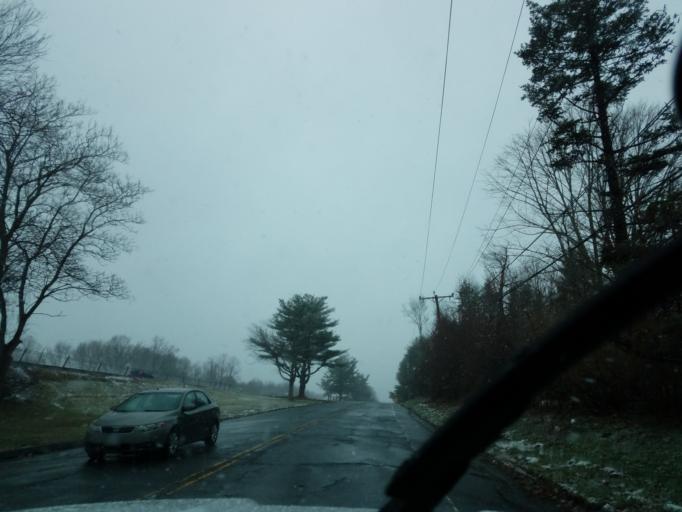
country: US
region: Connecticut
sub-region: New Haven County
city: Meriden
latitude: 41.5124
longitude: -72.7823
